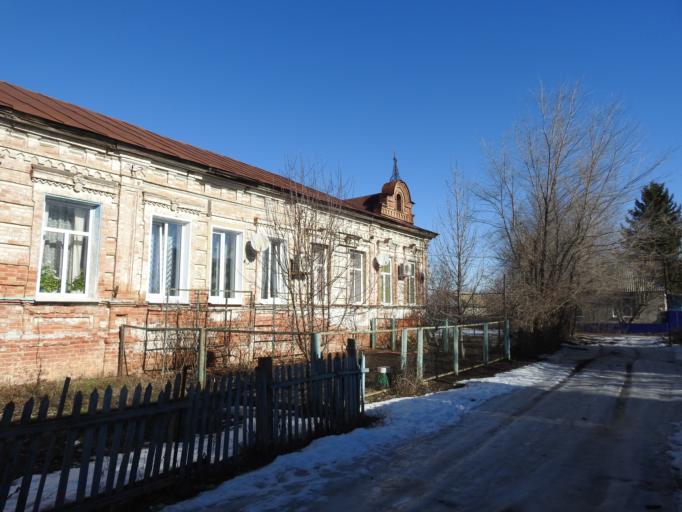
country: RU
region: Saratov
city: Yershov
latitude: 51.3398
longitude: 48.2258
